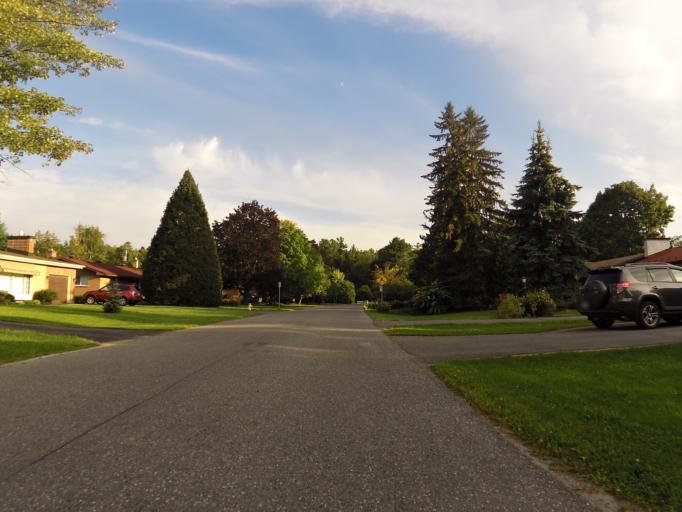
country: CA
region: Ontario
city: Bells Corners
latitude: 45.3281
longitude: -75.8137
